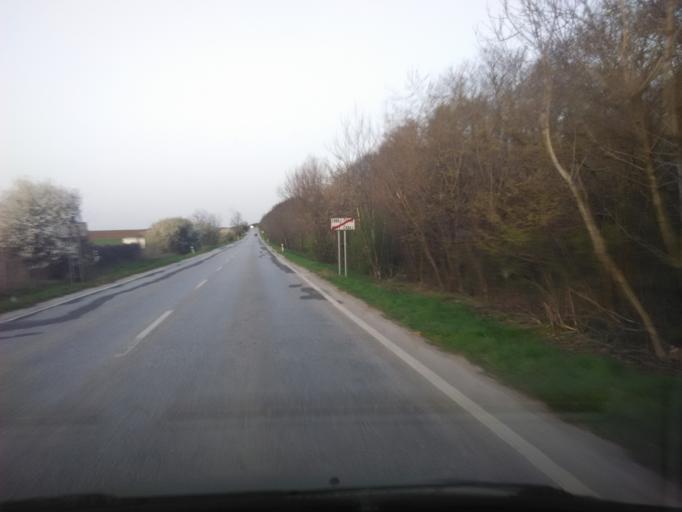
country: SK
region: Nitriansky
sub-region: Okres Nitra
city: Nitra
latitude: 48.2728
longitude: 18.0494
